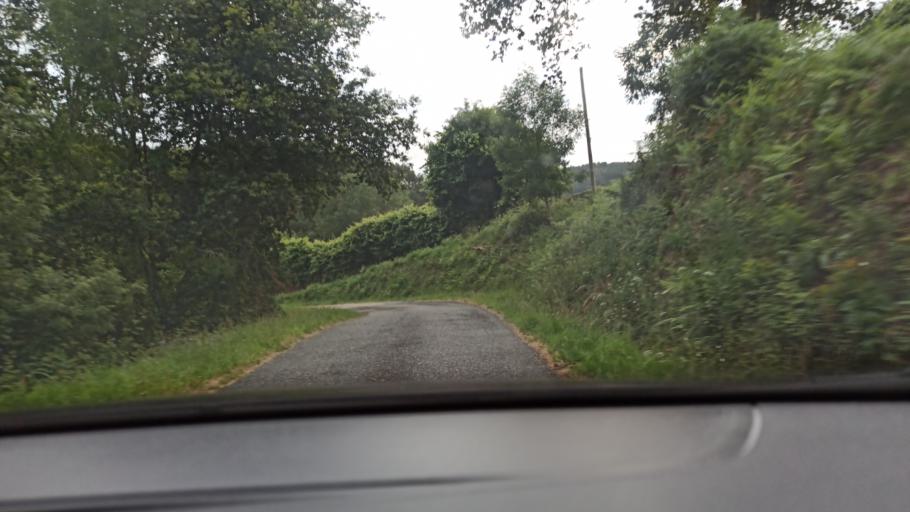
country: ES
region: Galicia
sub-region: Provincia da Coruna
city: Santiso
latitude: 42.8286
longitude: -8.1410
